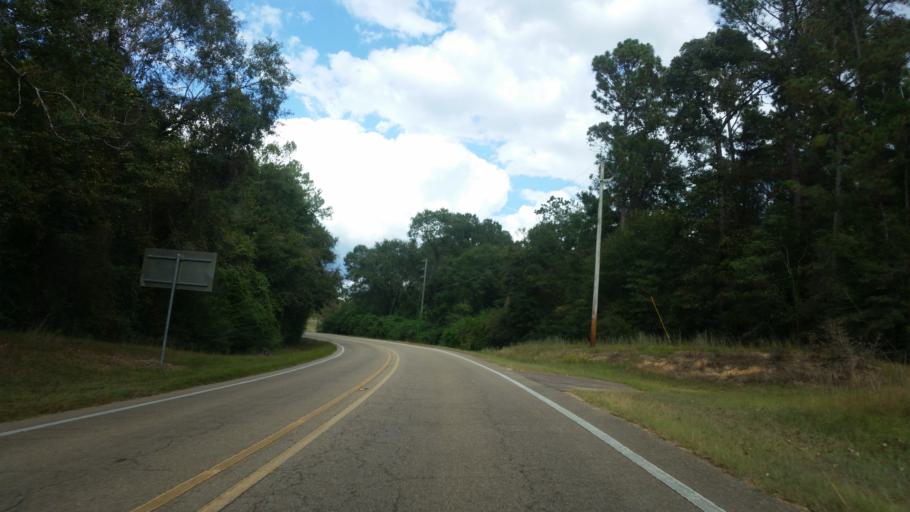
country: US
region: Mississippi
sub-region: Stone County
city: Wiggins
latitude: 30.8718
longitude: -89.1198
